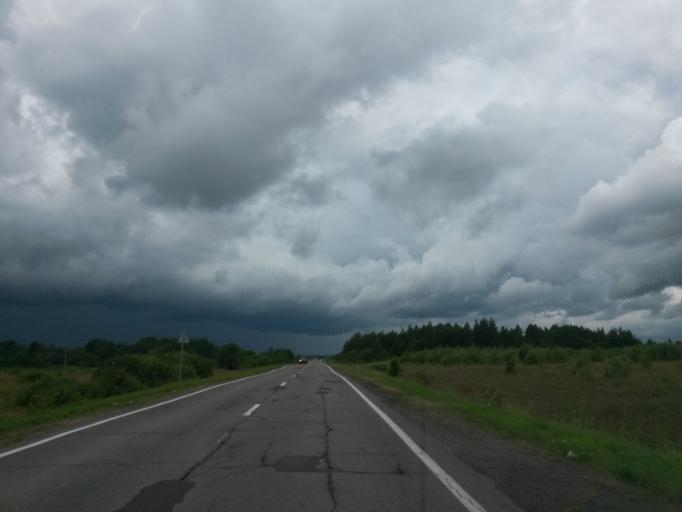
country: RU
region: Jaroslavl
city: Konstantinovskiy
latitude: 57.8652
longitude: 39.6082
